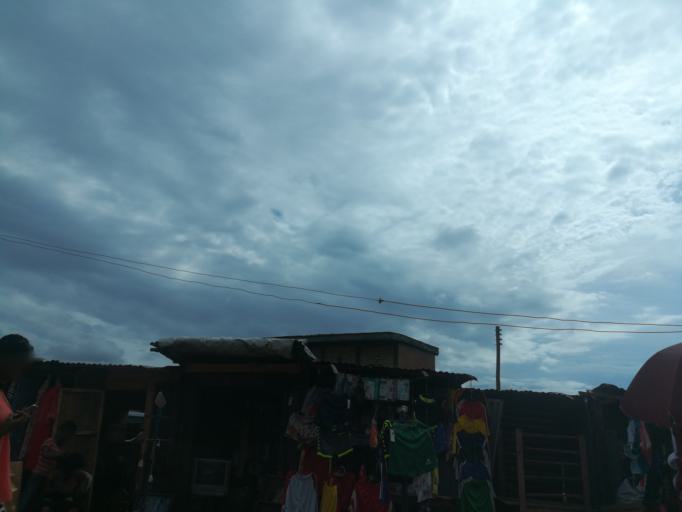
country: NG
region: Lagos
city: Agege
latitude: 6.6244
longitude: 3.3270
